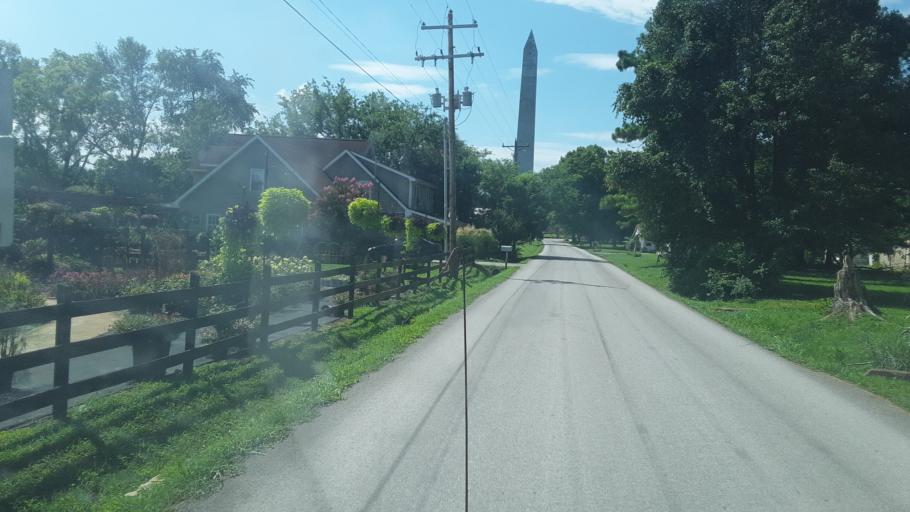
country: US
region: Kentucky
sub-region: Todd County
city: Elkton
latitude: 36.8457
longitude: -87.3010
